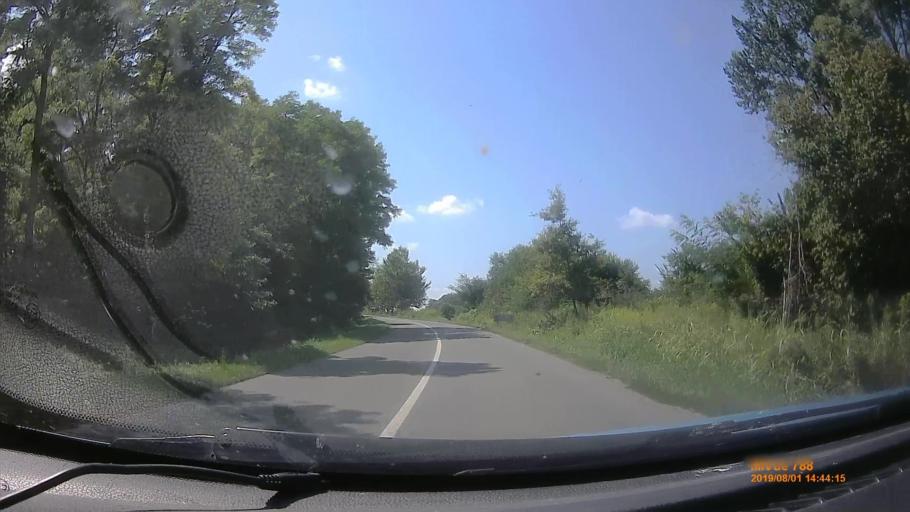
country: HR
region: Osjecko-Baranjska
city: Viljevo
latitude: 45.8418
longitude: 18.0798
